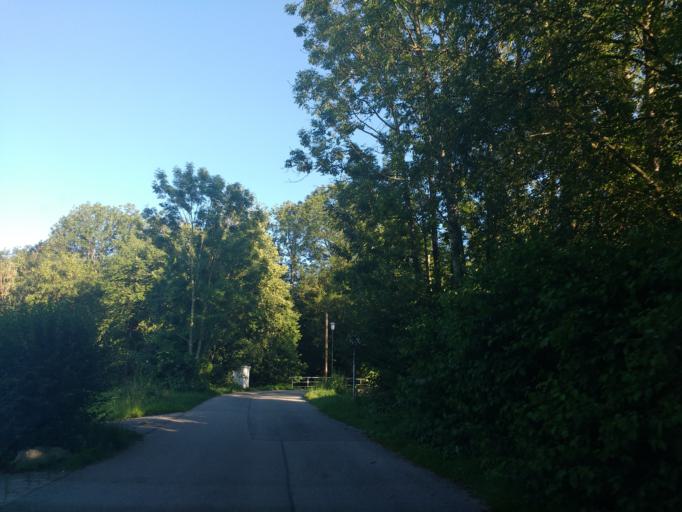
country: DE
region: Bavaria
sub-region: Upper Bavaria
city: Oberneukirchen
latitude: 48.1976
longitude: 12.4862
